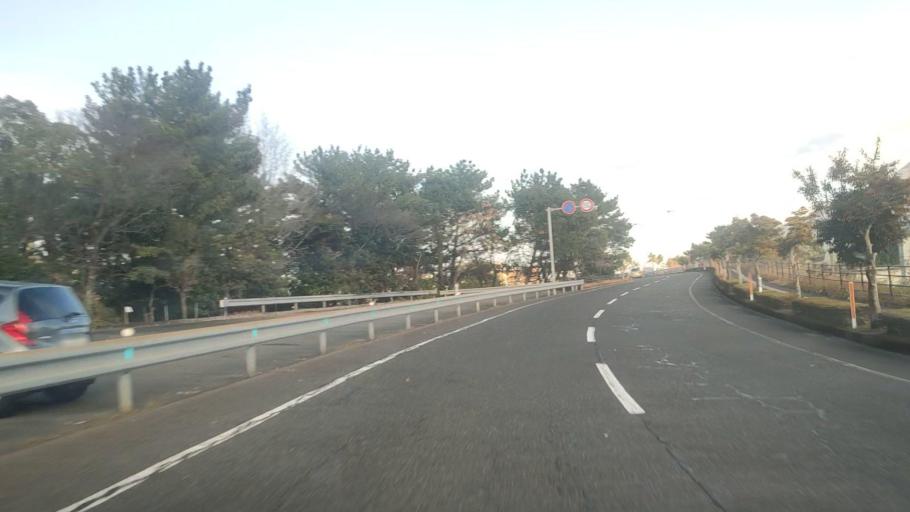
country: JP
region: Kagoshima
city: Kagoshima-shi
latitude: 31.6037
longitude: 130.5686
